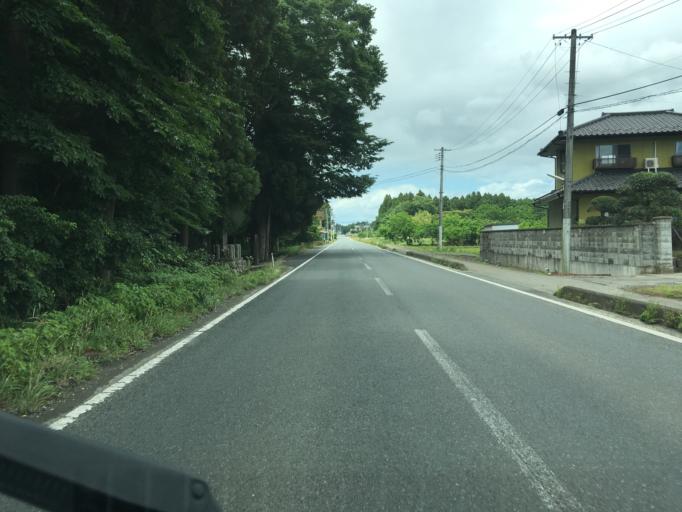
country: JP
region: Miyagi
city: Marumori
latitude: 37.7264
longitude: 140.9299
